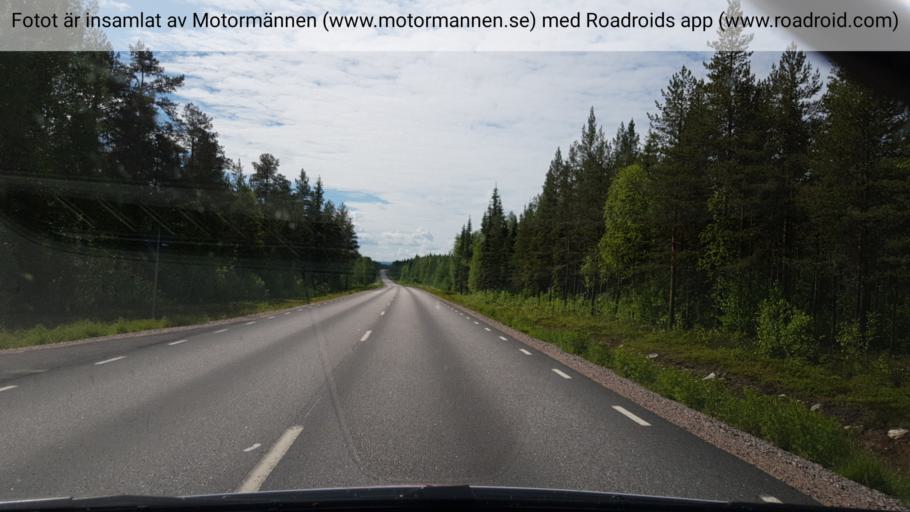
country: SE
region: Norrbotten
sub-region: Overtornea Kommun
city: OEvertornea
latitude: 66.5002
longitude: 23.7159
